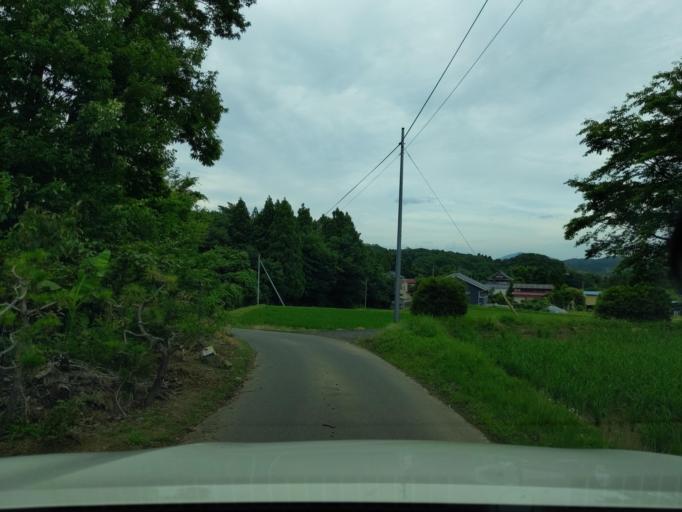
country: JP
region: Fukushima
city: Koriyama
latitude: 37.4347
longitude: 140.4058
